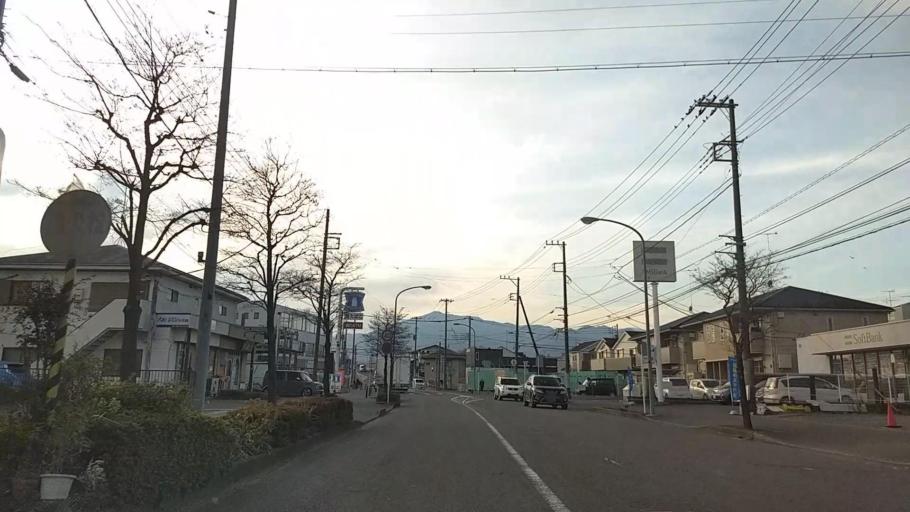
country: JP
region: Kanagawa
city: Atsugi
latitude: 35.4582
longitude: 139.3567
